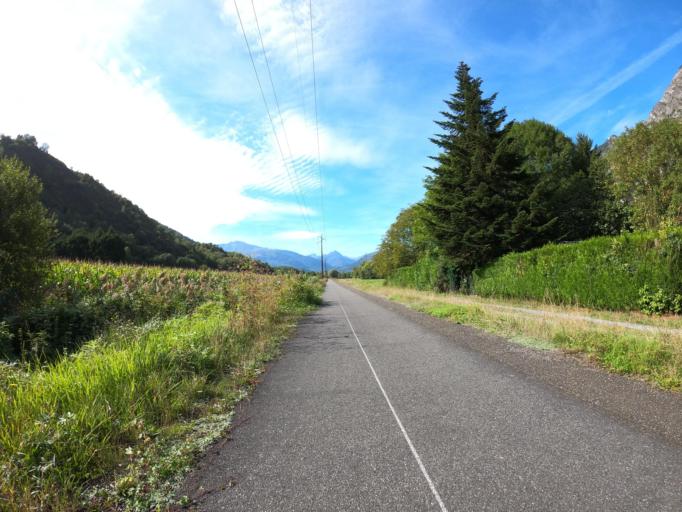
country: FR
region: Midi-Pyrenees
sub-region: Departement des Hautes-Pyrenees
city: Lourdes
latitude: 43.0484
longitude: -0.0505
